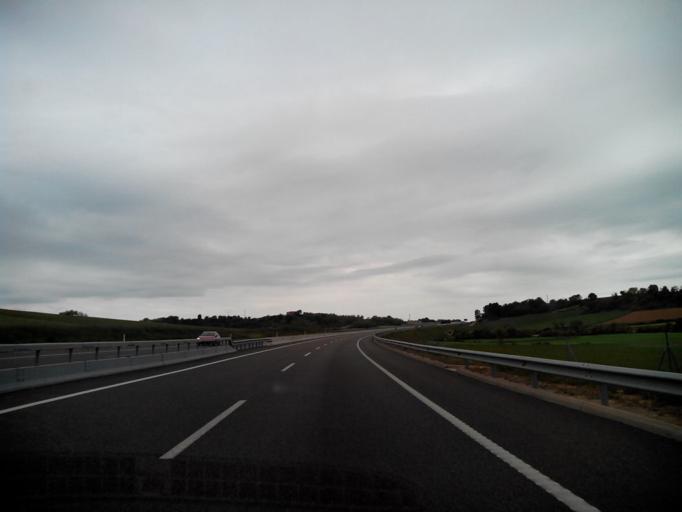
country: ES
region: Catalonia
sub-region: Provincia de Barcelona
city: Pujalt
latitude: 41.7338
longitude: 1.4084
